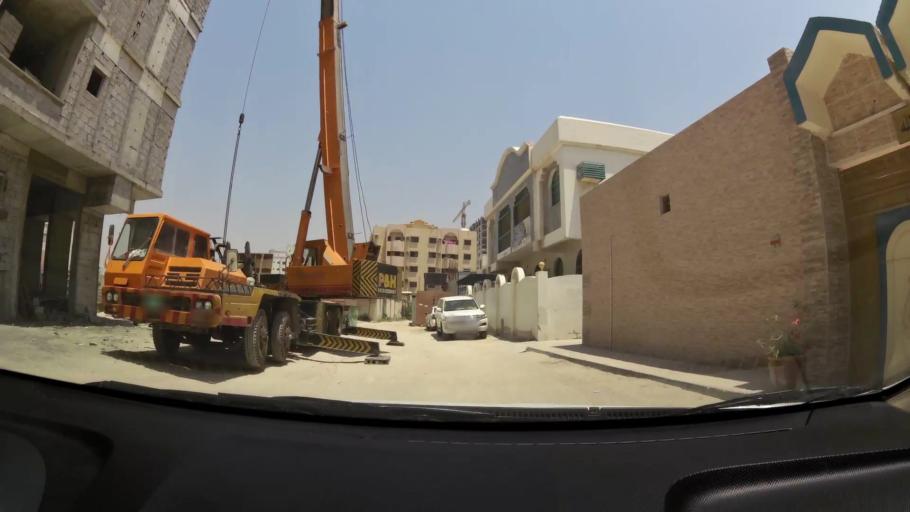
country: AE
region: Ajman
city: Ajman
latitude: 25.4083
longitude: 55.4355
